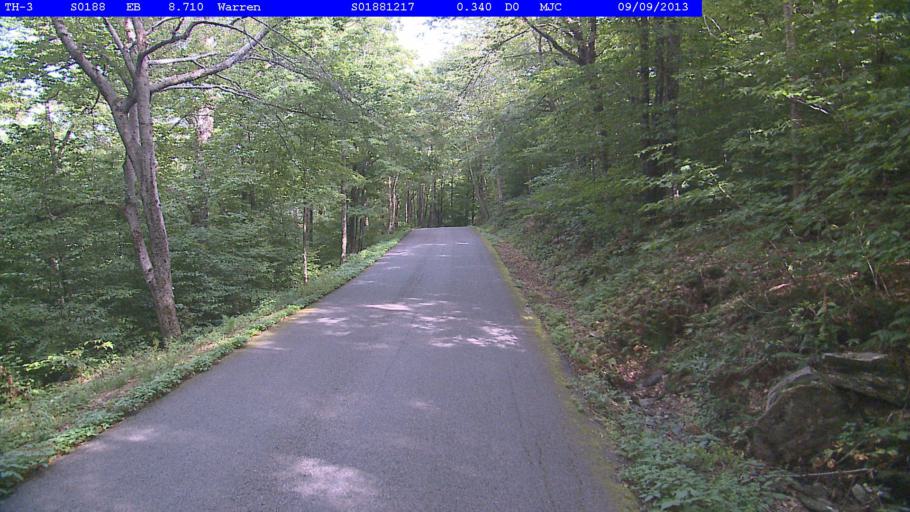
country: US
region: Vermont
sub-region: Addison County
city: Bristol
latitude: 44.0941
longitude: -72.9162
